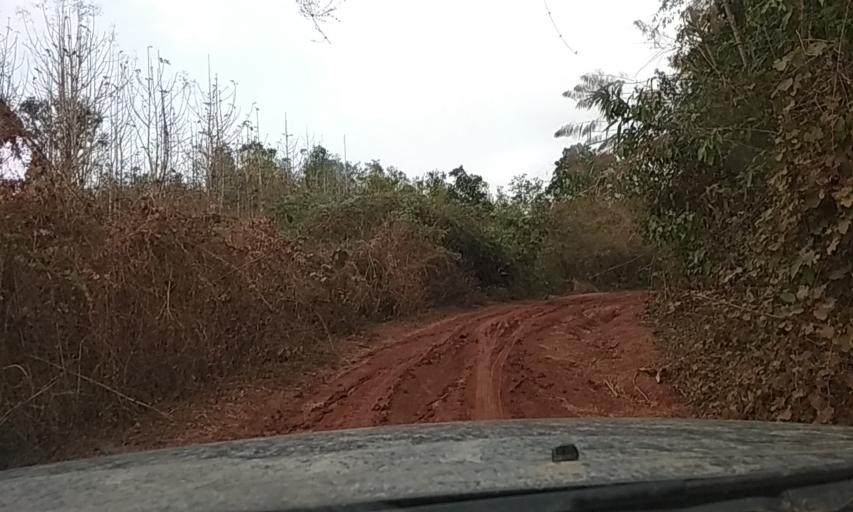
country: TH
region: Nan
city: Mae Charim
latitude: 18.4398
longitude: 101.1869
